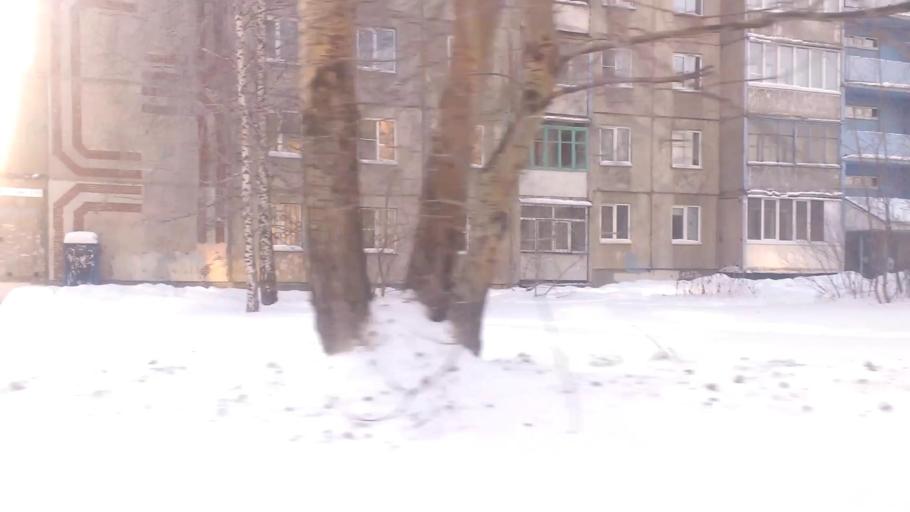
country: RU
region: Altai Krai
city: Novosilikatnyy
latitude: 53.3745
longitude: 83.6654
